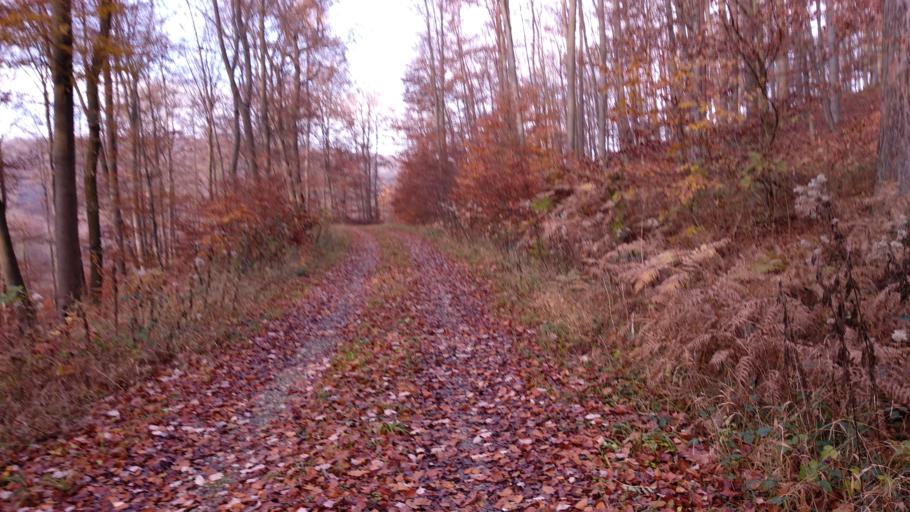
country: DE
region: North Rhine-Westphalia
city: Beverungen
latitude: 51.6561
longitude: 9.3252
